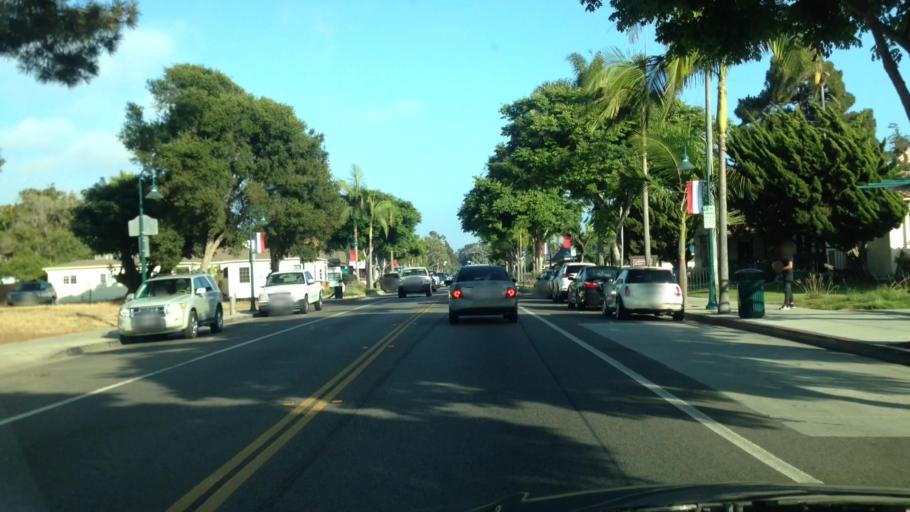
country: US
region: California
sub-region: Santa Barbara County
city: Carpinteria
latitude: 34.3979
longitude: -119.5172
